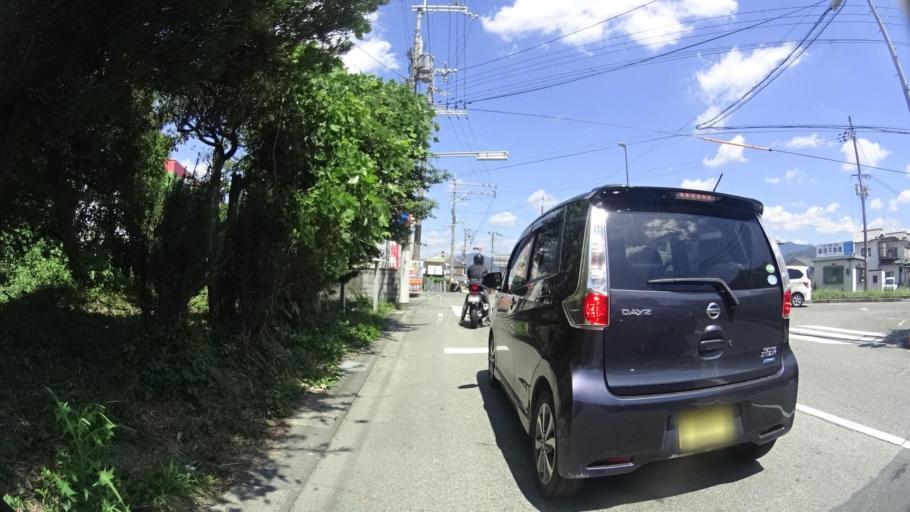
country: JP
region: Kyoto
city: Kameoka
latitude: 35.0082
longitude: 135.5774
